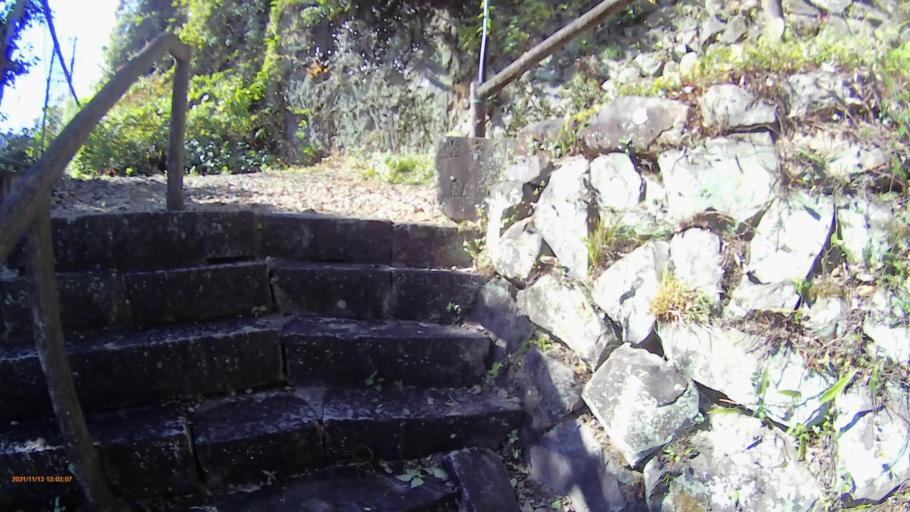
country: JP
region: Gifu
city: Inuyama
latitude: 35.4214
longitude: 136.9637
